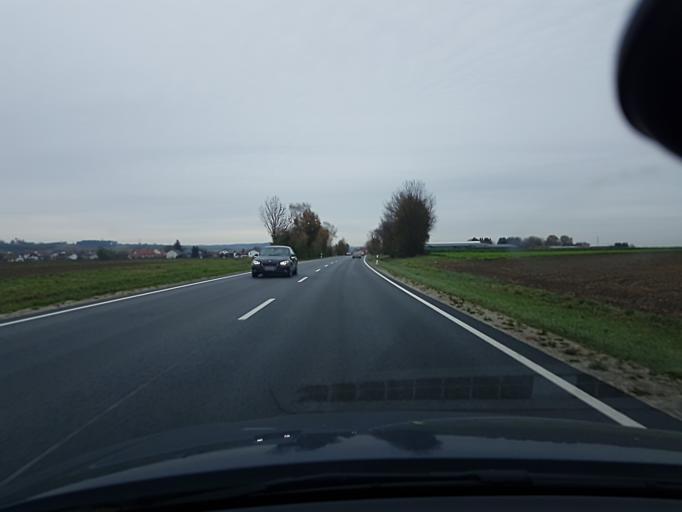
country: DE
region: Bavaria
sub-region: Lower Bavaria
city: Essenbach
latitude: 48.6067
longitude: 12.2076
